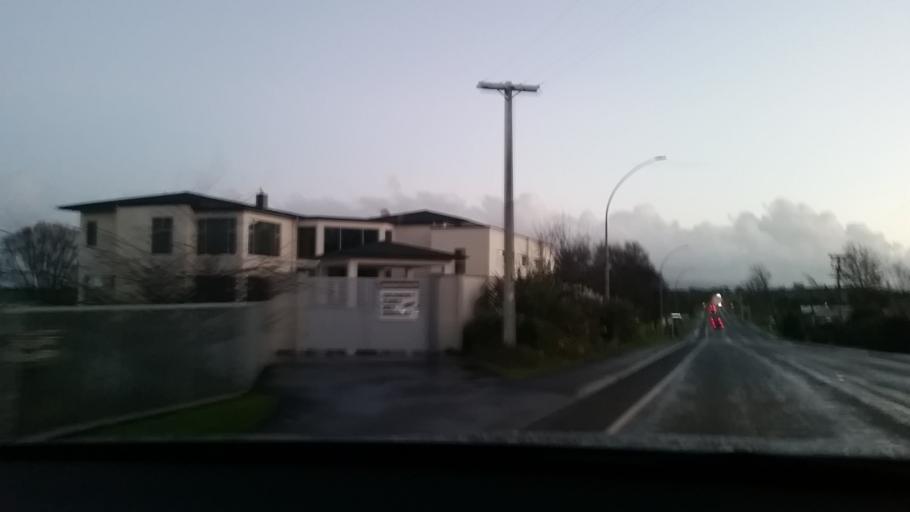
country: NZ
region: Waikato
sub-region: Hamilton City
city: Hamilton
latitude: -37.8043
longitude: 175.2429
